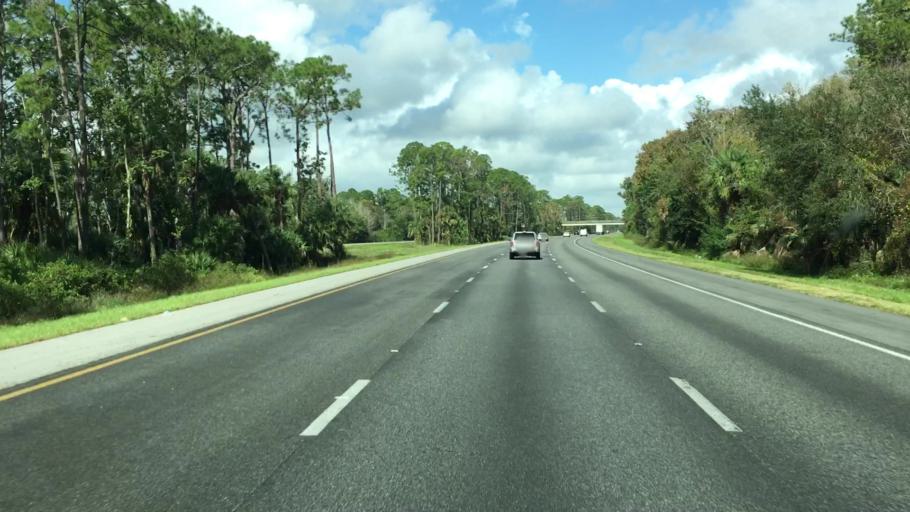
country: US
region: Florida
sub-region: Volusia County
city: Glencoe
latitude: 29.0430
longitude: -81.0062
